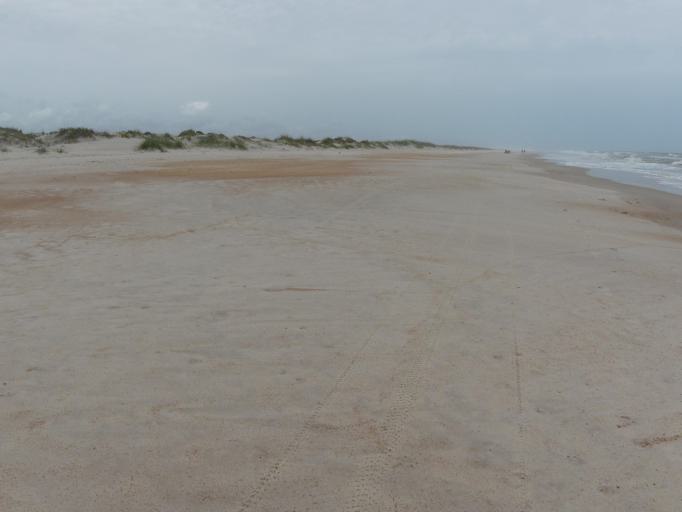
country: US
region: Florida
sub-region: Saint Johns County
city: Saint Augustine
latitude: 29.8906
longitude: -81.2747
